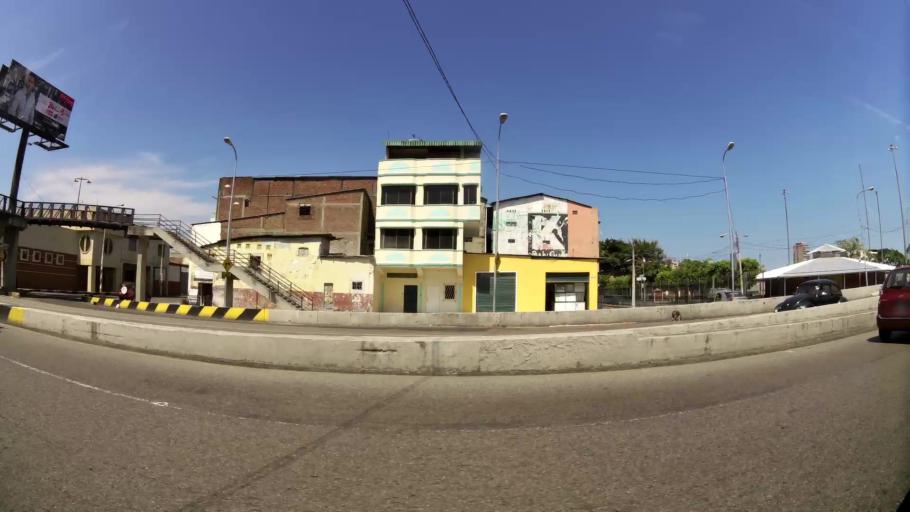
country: EC
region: Guayas
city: Guayaquil
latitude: -2.1834
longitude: -79.8864
